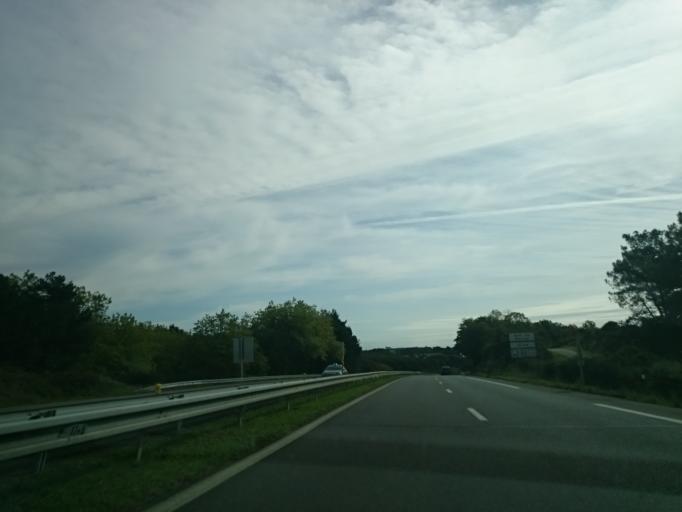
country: FR
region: Brittany
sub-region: Departement du Morbihan
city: Muzillac
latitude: 47.5490
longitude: -2.4531
